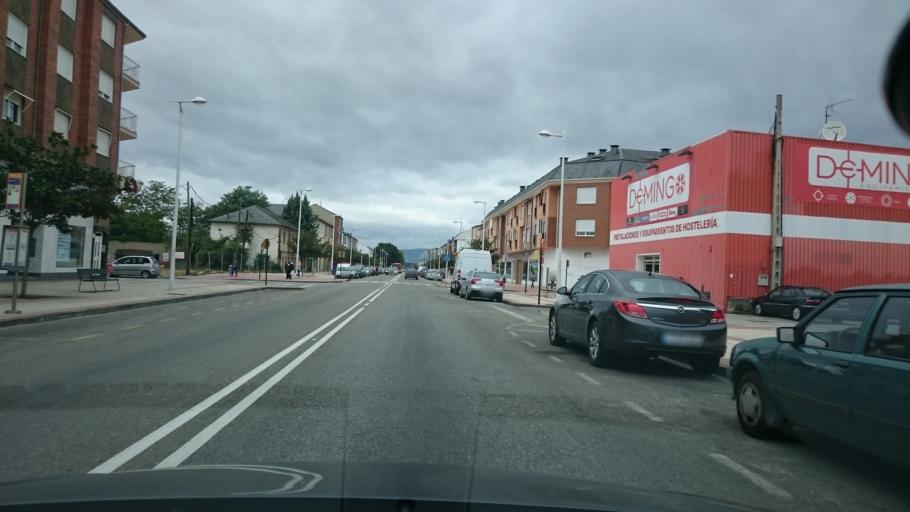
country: ES
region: Castille and Leon
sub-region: Provincia de Leon
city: Ponferrada
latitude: 42.5605
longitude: -6.6256
